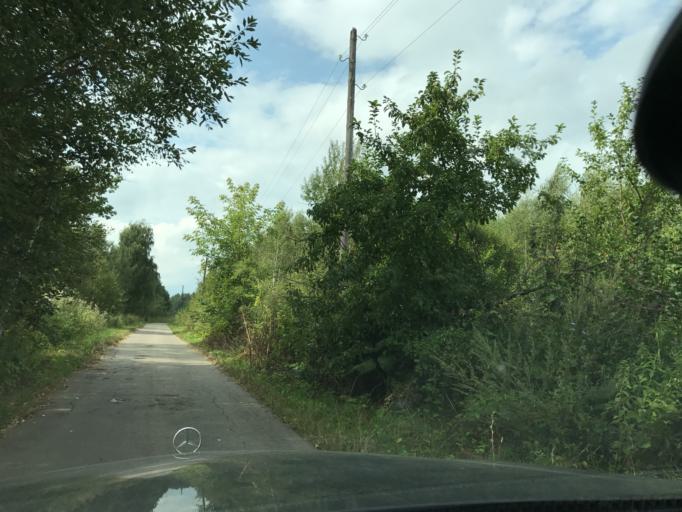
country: RU
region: Nizjnij Novgorod
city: Vacha
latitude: 55.9764
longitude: 42.7604
